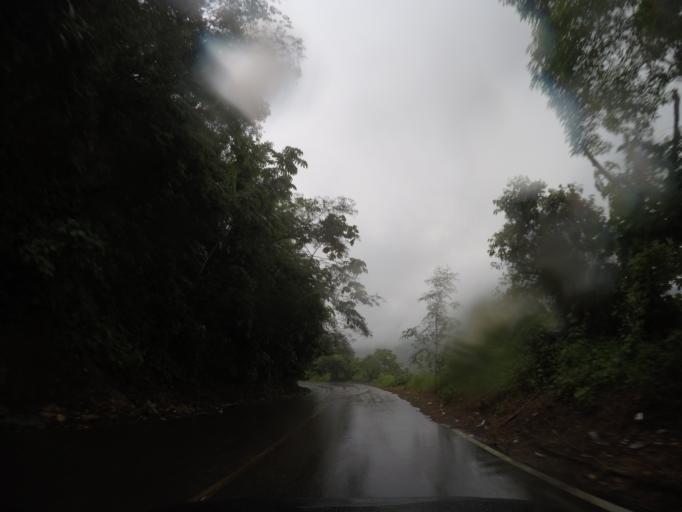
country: MX
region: Oaxaca
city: San Gabriel Mixtepec
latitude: 16.0774
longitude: -97.0868
